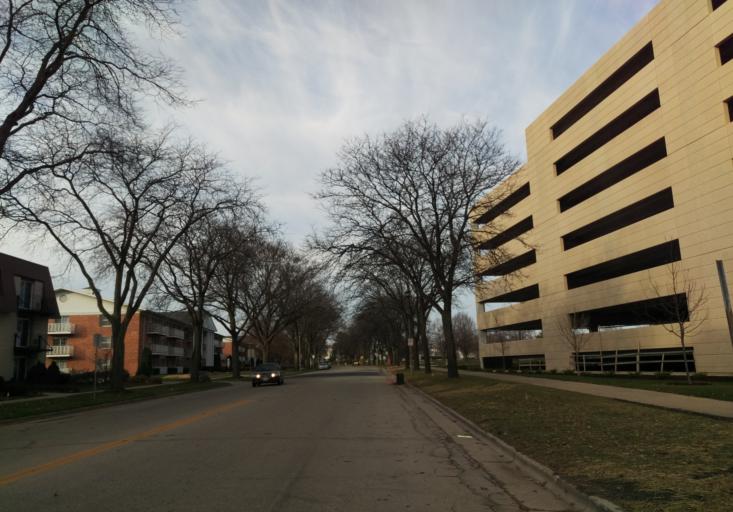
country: US
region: Wisconsin
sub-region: Dane County
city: Shorewood Hills
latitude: 43.0729
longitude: -89.4607
